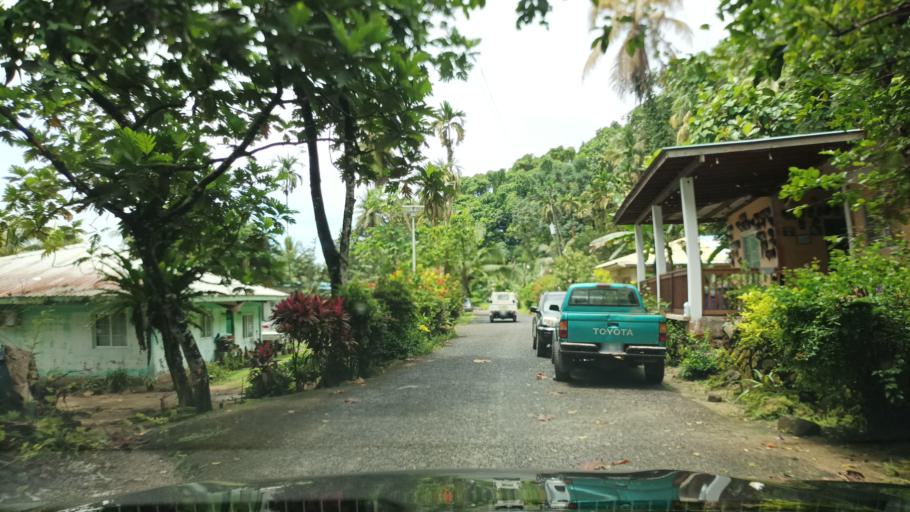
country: FM
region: Pohnpei
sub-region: Kolonia Municipality
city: Kolonia
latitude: 6.9720
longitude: 158.2230
